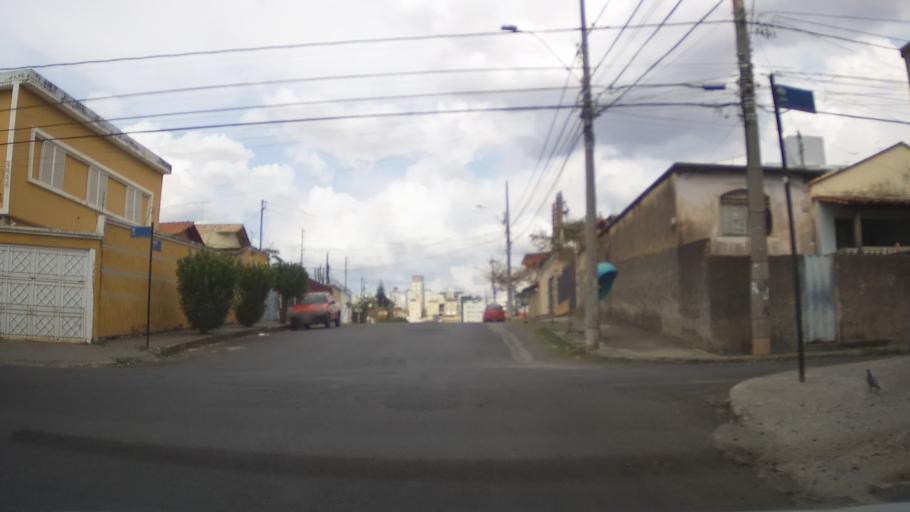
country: BR
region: Minas Gerais
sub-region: Belo Horizonte
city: Belo Horizonte
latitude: -19.8879
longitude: -43.9391
